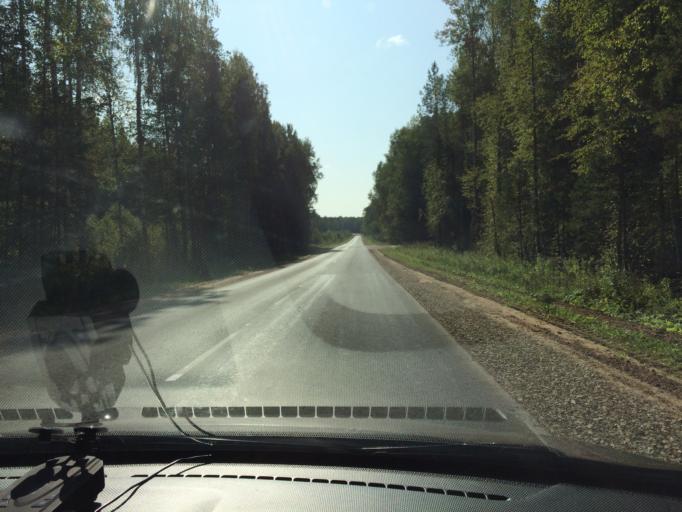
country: RU
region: Mariy-El
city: Surok
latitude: 56.5569
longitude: 48.3100
